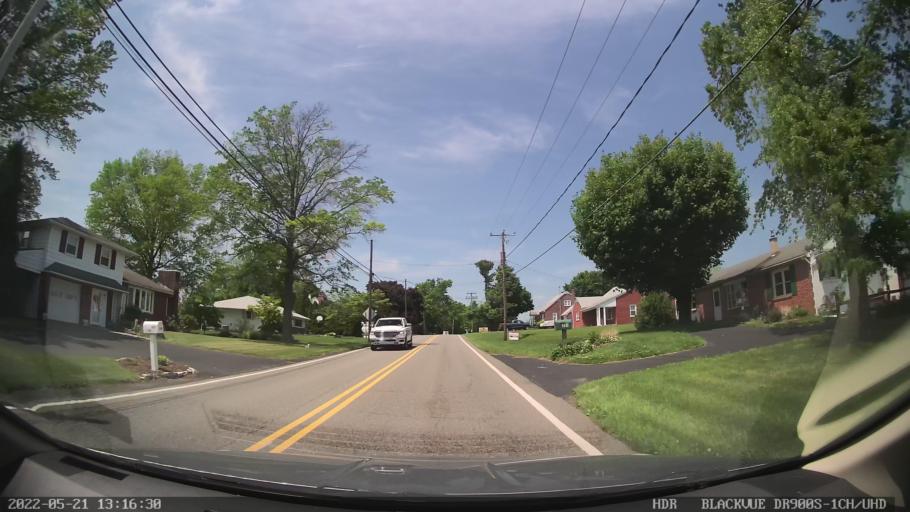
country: US
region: Pennsylvania
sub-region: Montgomery County
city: Gilbertsville
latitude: 40.3516
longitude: -75.5854
